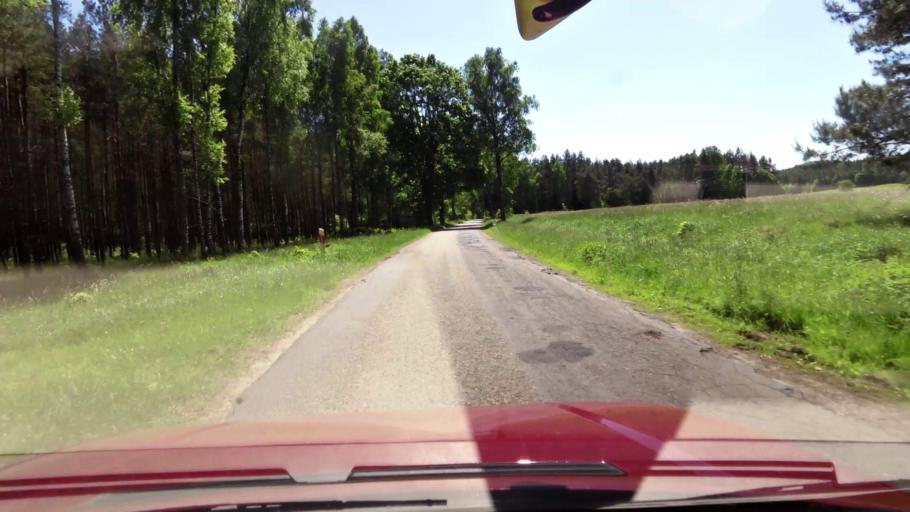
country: PL
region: West Pomeranian Voivodeship
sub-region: Powiat koszalinski
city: Bobolice
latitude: 54.0476
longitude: 16.5901
